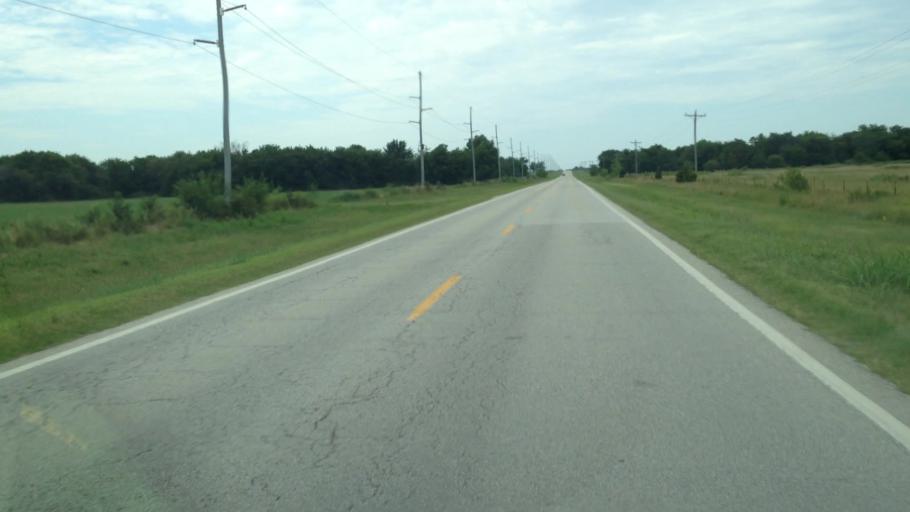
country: US
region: Kansas
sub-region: Labette County
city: Chetopa
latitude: 36.9065
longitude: -95.0896
